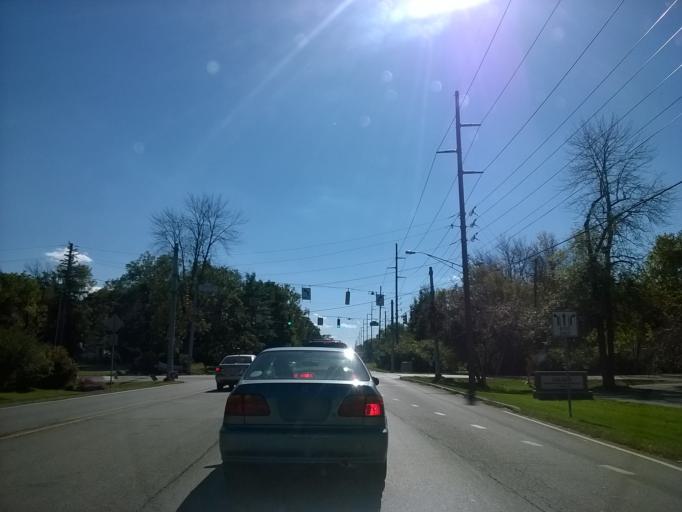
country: US
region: Indiana
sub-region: Marion County
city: Broad Ripple
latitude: 39.8982
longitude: -86.0823
